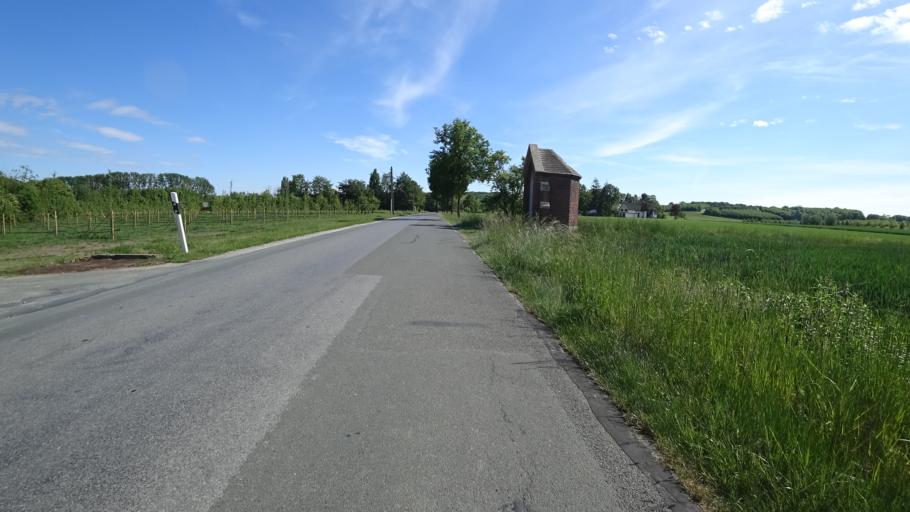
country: DE
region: North Rhine-Westphalia
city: Oelde
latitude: 51.8160
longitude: 8.2221
